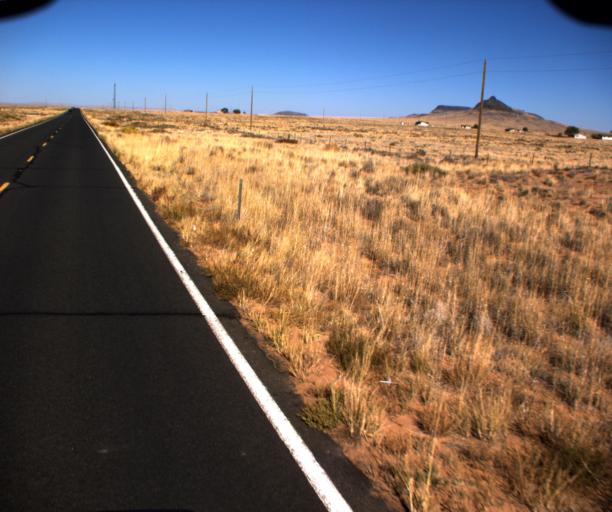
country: US
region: Arizona
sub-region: Navajo County
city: Dilkon
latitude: 35.5048
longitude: -110.4361
